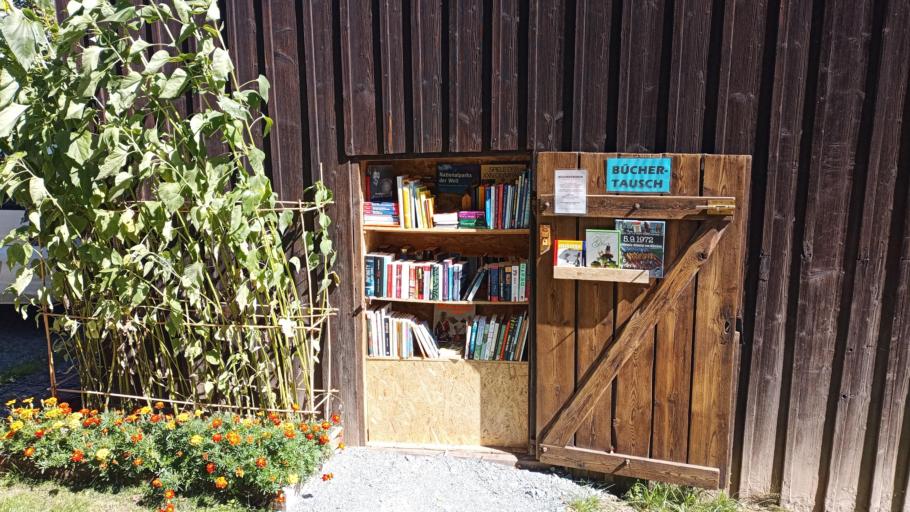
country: DE
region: Saxony
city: Gornau
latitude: 50.7807
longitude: 13.0522
